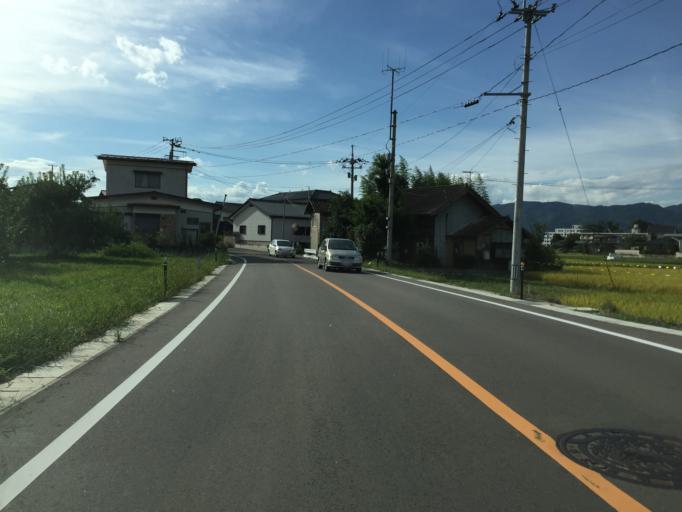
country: JP
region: Fukushima
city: Hobaramachi
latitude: 37.8130
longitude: 140.5268
